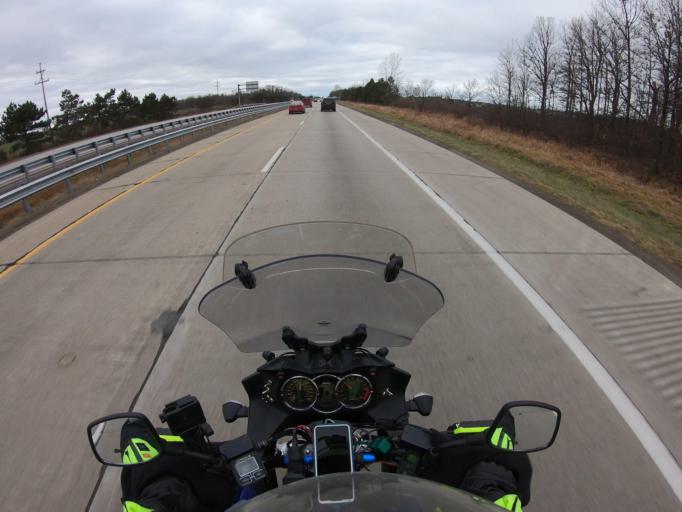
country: US
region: Michigan
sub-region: Bay County
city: Bay City
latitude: 43.5961
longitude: -83.9584
